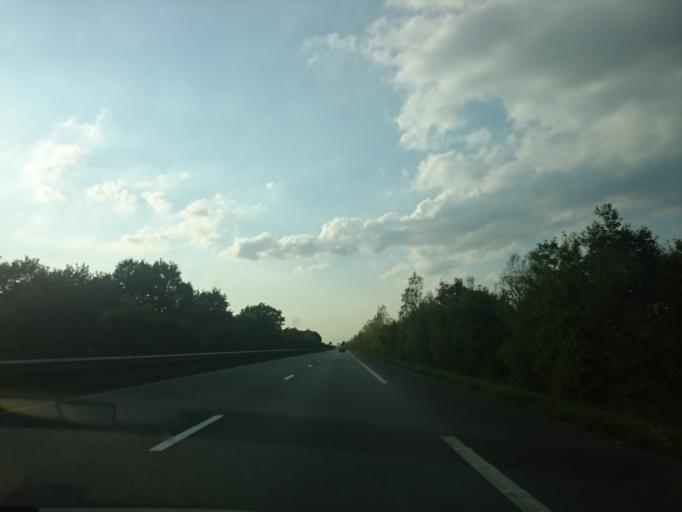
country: FR
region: Pays de la Loire
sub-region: Departement de la Loire-Atlantique
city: La Chapelle-Launay
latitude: 47.3876
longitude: -1.9825
